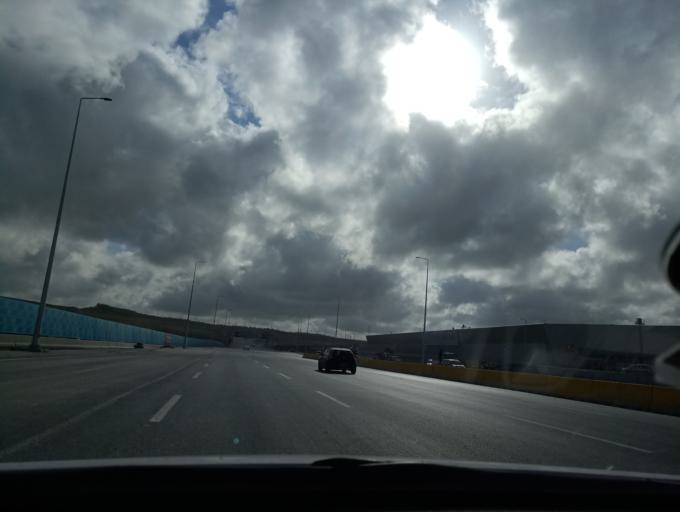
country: TR
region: Istanbul
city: Durusu
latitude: 41.2521
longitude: 28.7390
